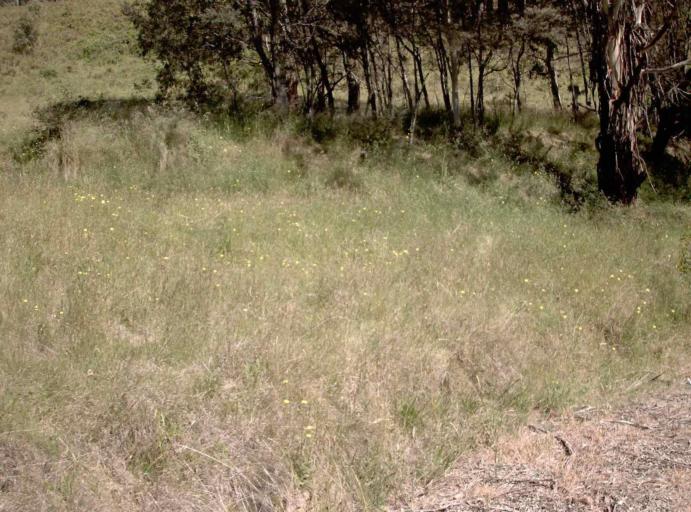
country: AU
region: New South Wales
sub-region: Bombala
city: Bombala
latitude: -37.0660
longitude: 148.7974
